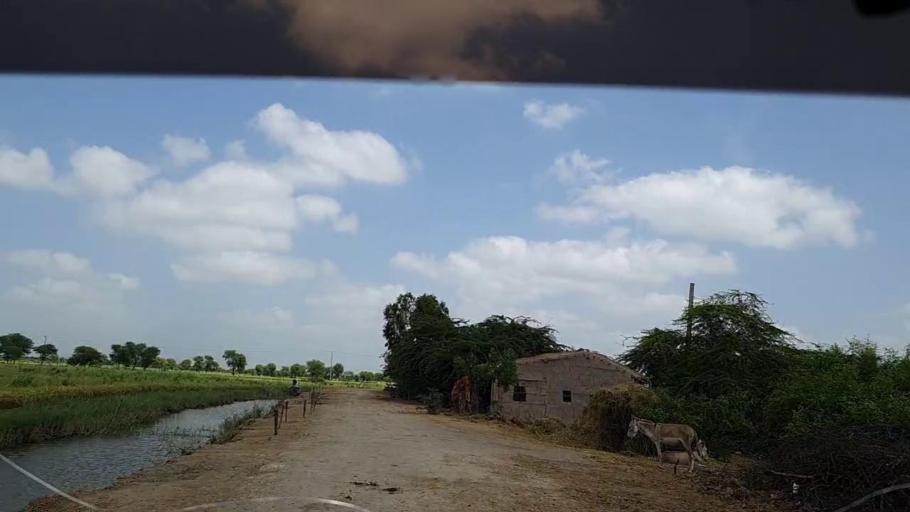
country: PK
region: Sindh
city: Badin
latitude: 24.5829
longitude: 68.7658
